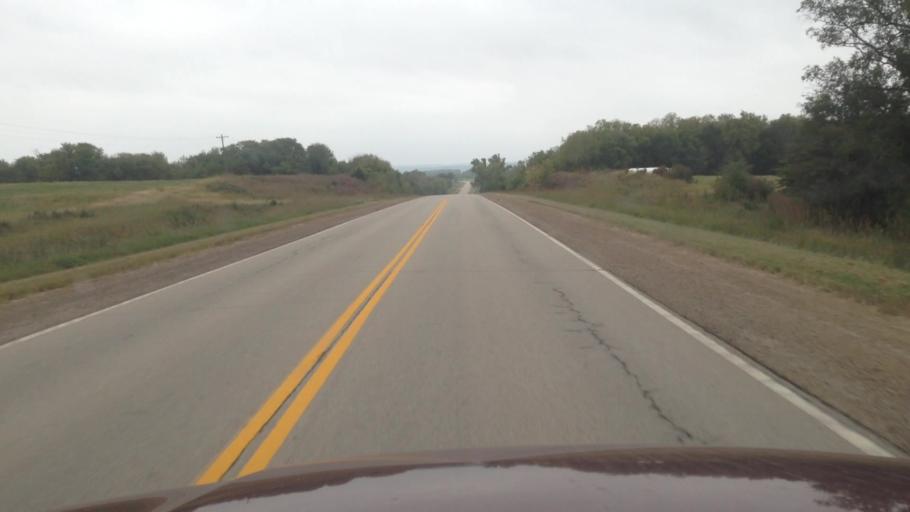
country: US
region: Kansas
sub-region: Jefferson County
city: Oskaloosa
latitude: 39.1163
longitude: -95.4838
